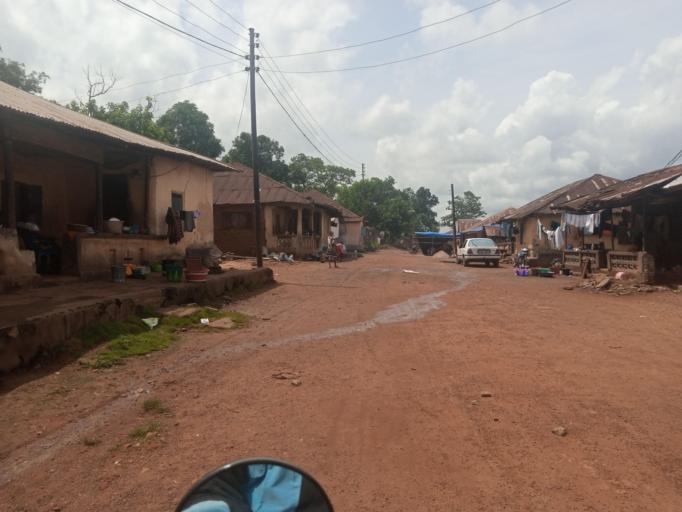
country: SL
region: Southern Province
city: Bo
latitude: 7.9687
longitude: -11.7344
